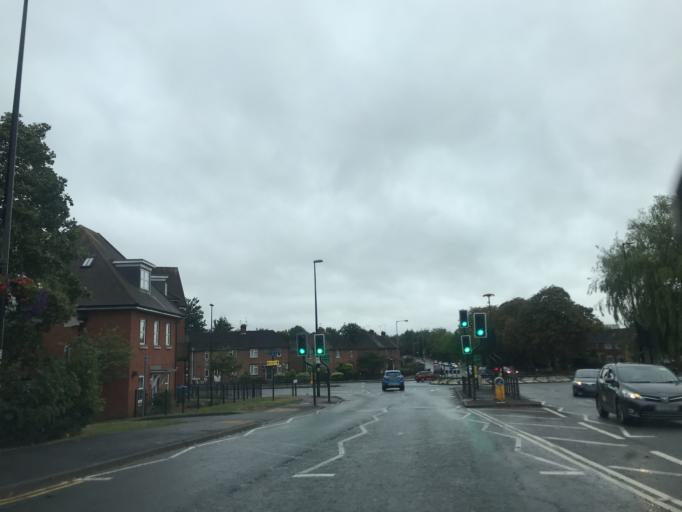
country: GB
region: England
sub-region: Buckinghamshire
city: Aylesbury
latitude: 51.8181
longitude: -0.8184
